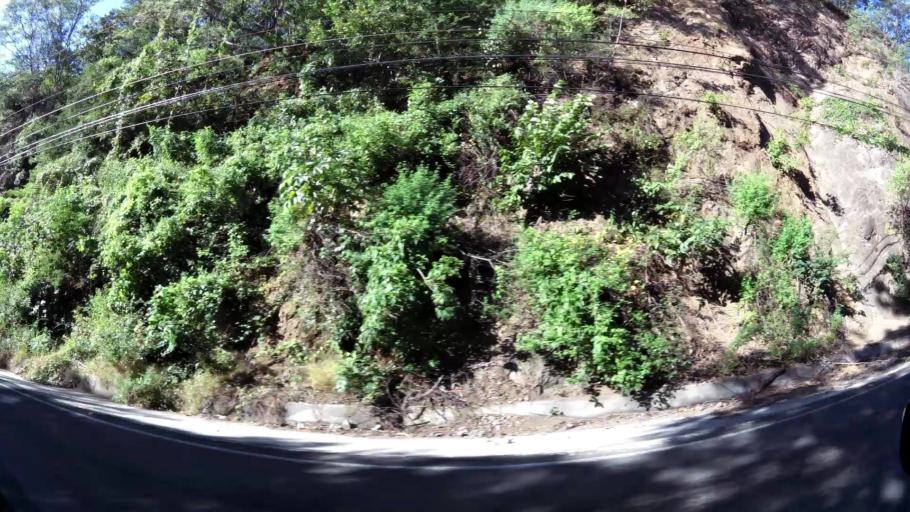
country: CR
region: Guanacaste
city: Belen
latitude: 10.3662
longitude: -85.7574
